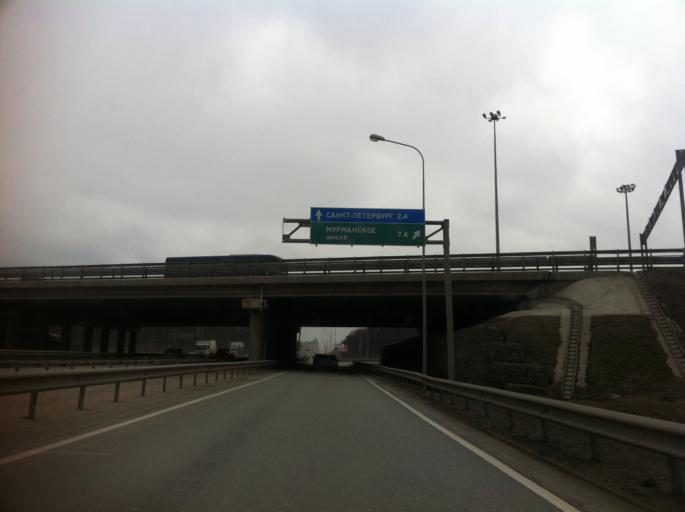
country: RU
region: St.-Petersburg
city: Krasnogvargeisky
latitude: 59.9463
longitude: 30.5423
